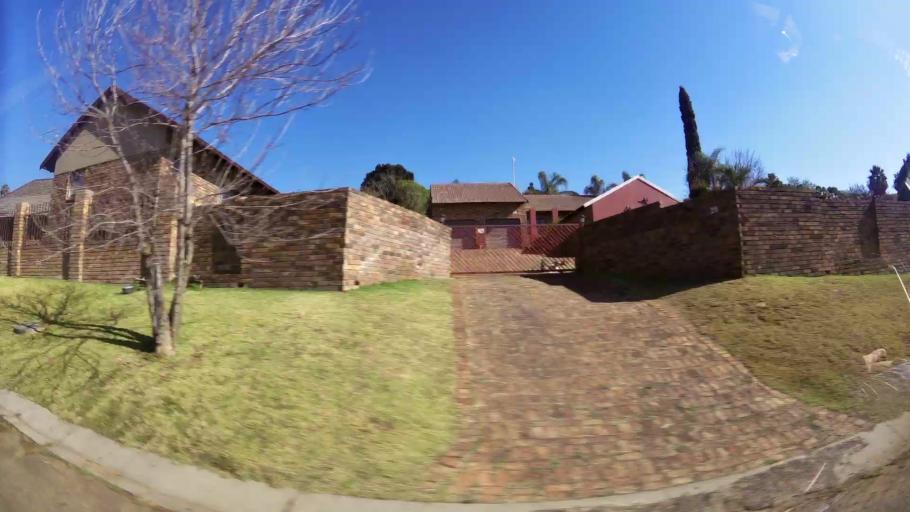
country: ZA
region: Mpumalanga
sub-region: Nkangala District Municipality
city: Witbank
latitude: -25.8736
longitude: 29.2532
